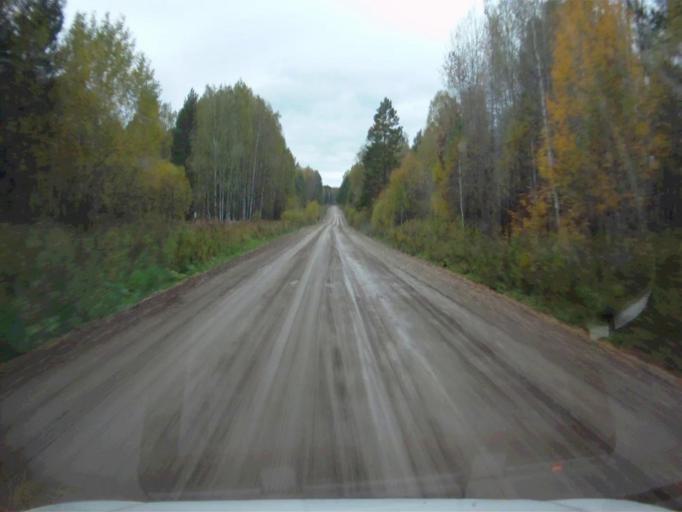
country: RU
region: Chelyabinsk
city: Nyazepetrovsk
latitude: 56.0927
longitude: 59.4090
